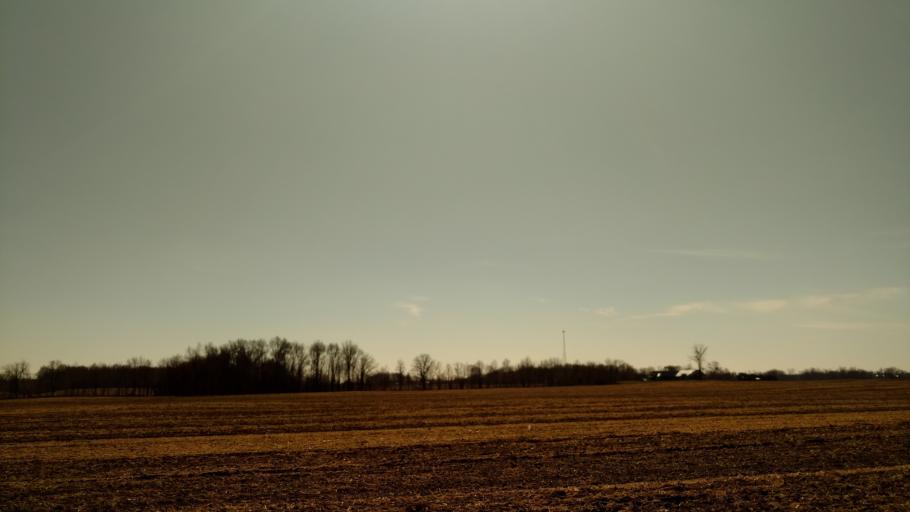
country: US
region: Ohio
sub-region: Union County
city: Richwood
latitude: 40.5266
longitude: -83.3202
